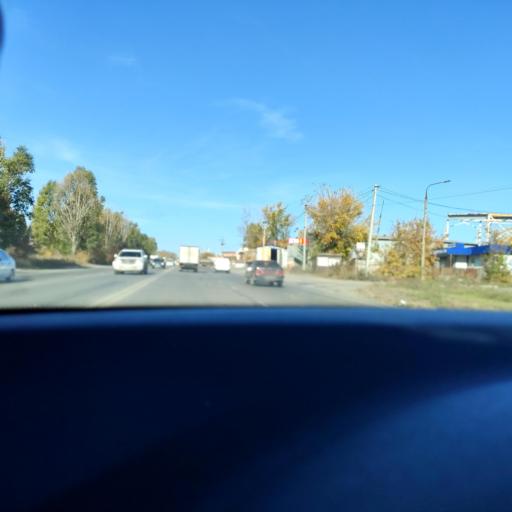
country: RU
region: Samara
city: Petra-Dubrava
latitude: 53.2624
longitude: 50.2882
